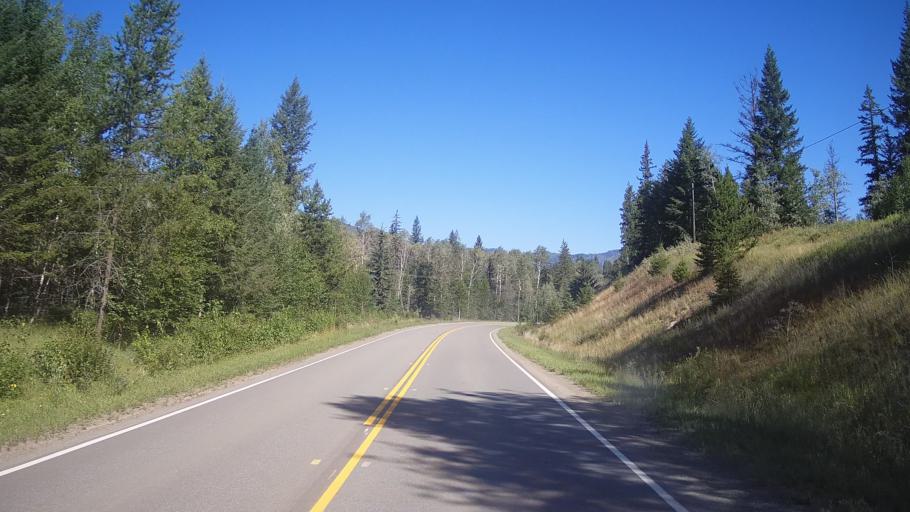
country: CA
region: British Columbia
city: Kamloops
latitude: 51.4401
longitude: -120.2108
